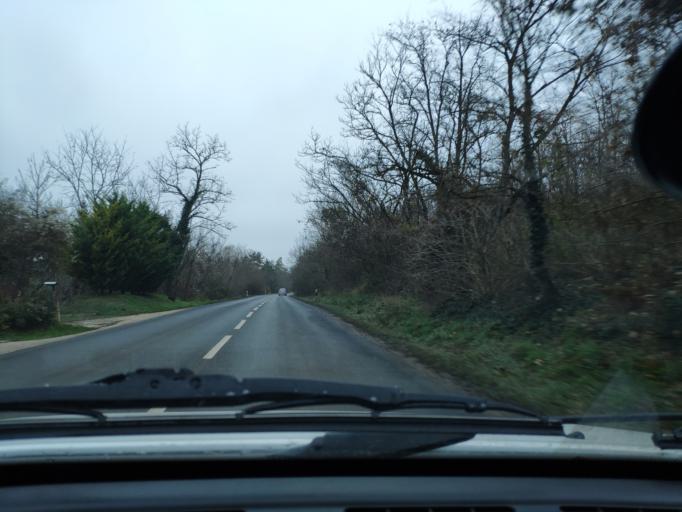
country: HU
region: Pest
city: Biatorbagy
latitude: 47.4420
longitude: 18.8177
